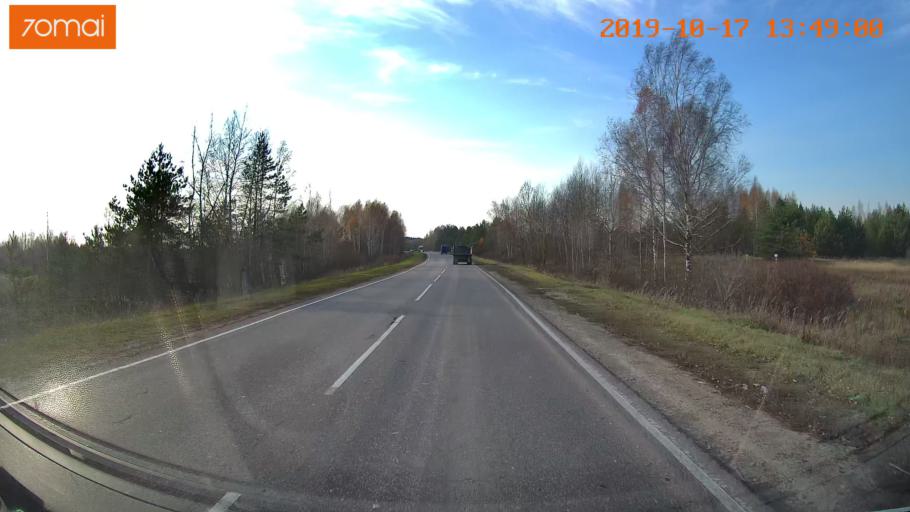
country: RU
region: Rjazan
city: Tuma
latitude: 55.1471
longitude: 40.4436
